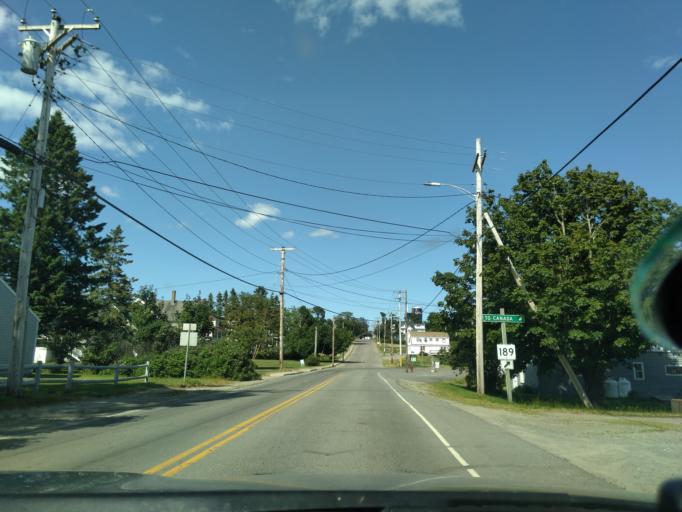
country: US
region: Maine
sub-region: Washington County
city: Eastport
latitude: 44.8571
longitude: -66.9913
